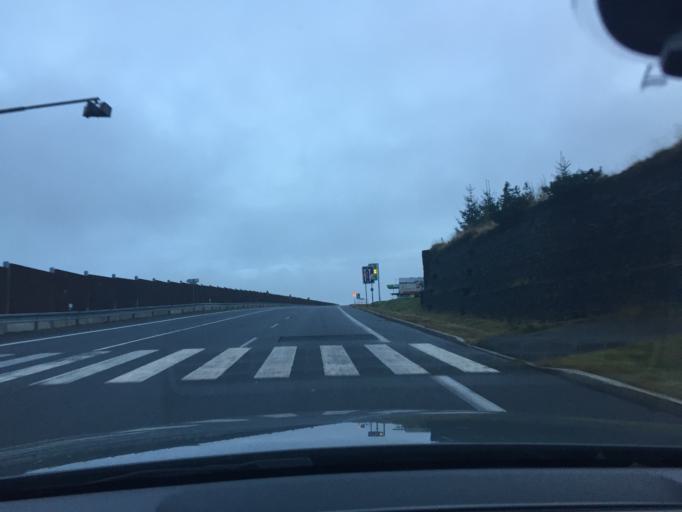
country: DE
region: Saxony
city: Altenberg
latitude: 50.7336
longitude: 13.7603
